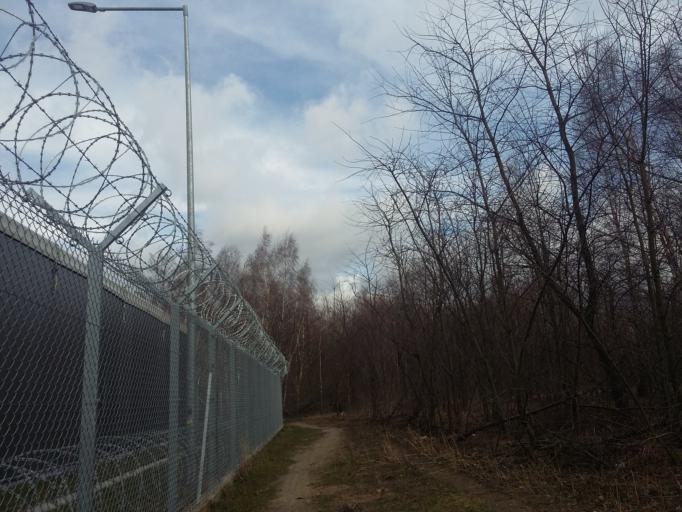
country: PL
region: Lodz Voivodeship
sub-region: Powiat pabianicki
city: Ksawerow
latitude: 51.7270
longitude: 19.4051
